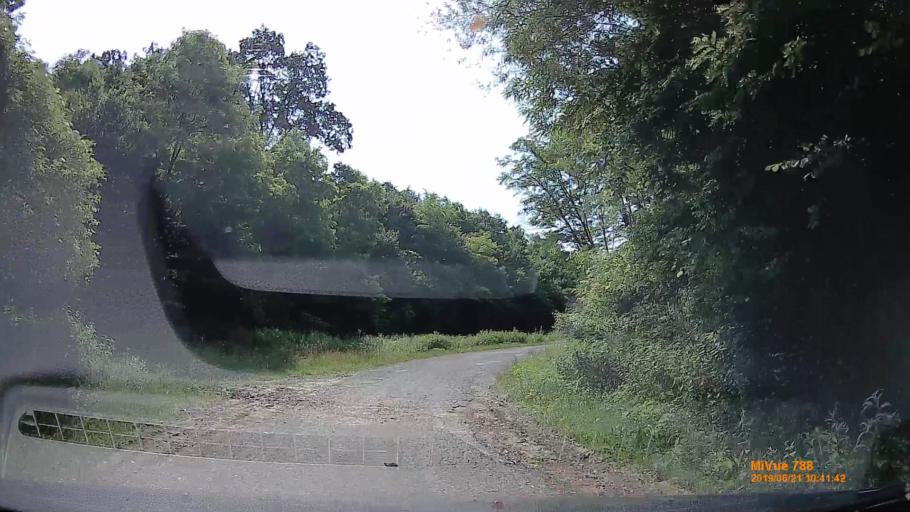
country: HU
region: Baranya
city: Buekkoesd
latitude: 46.1332
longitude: 18.0034
